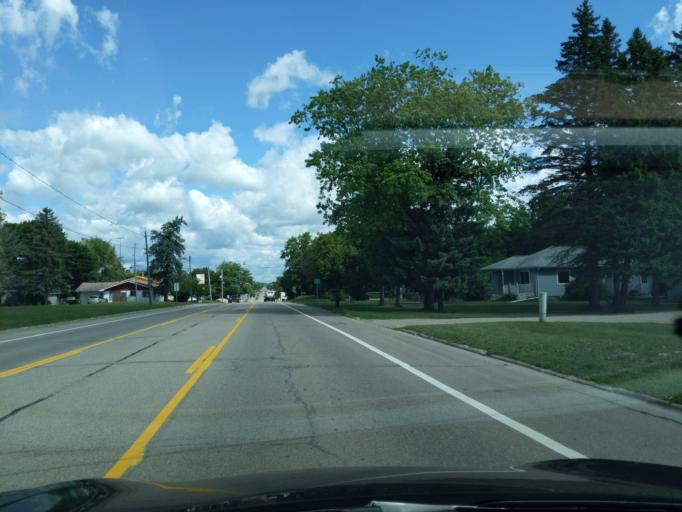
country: US
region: Michigan
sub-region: Clare County
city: Clare
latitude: 43.8130
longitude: -84.7683
